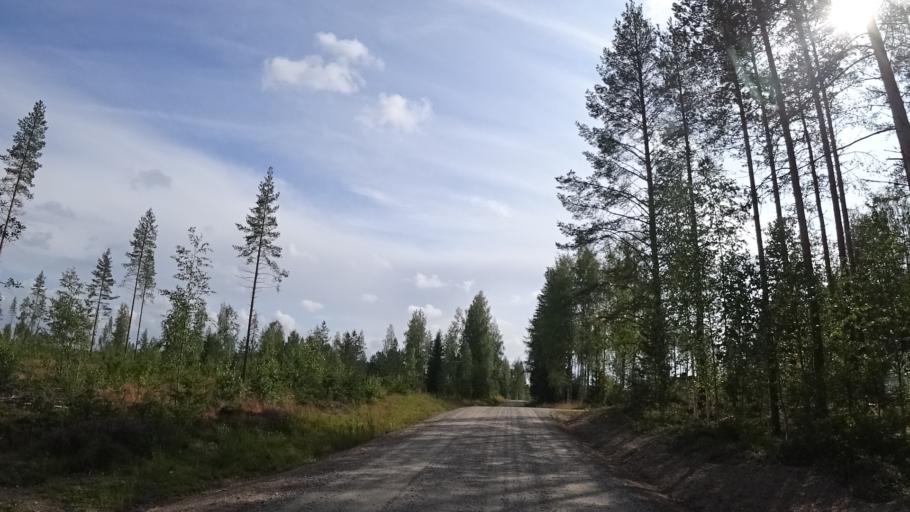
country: FI
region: North Karelia
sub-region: Pielisen Karjala
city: Lieksa
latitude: 63.5887
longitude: 30.1351
